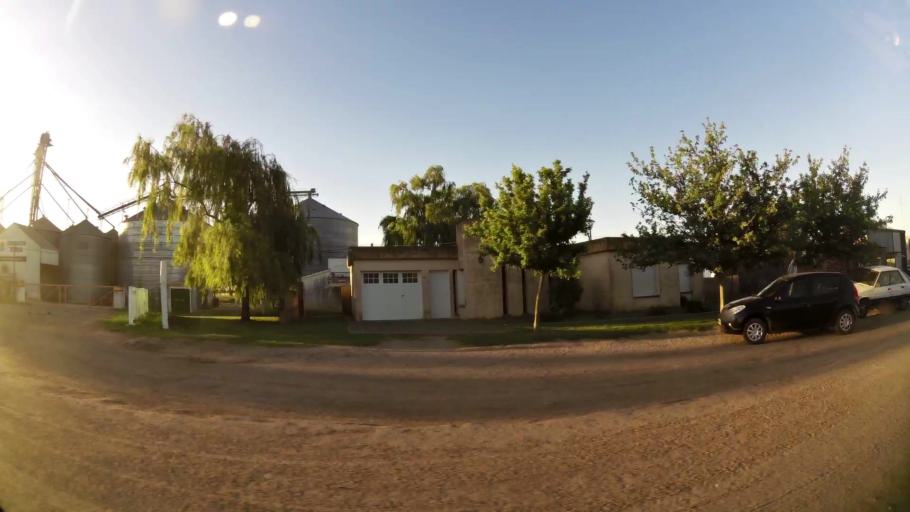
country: AR
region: Cordoba
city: La Playosa
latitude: -32.1025
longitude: -63.0354
